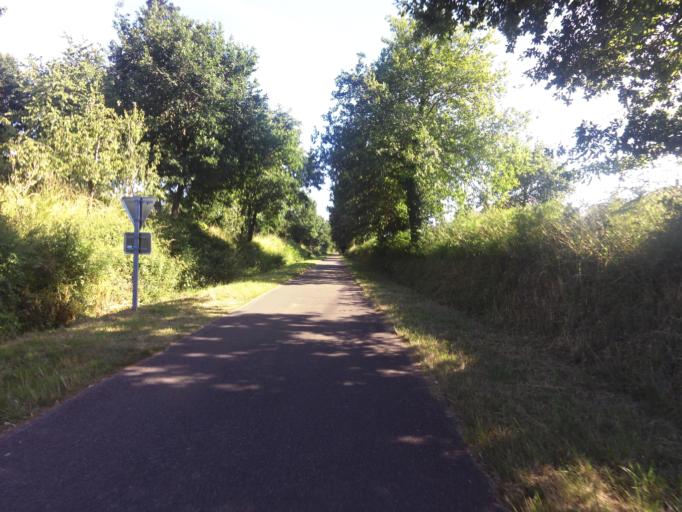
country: FR
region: Brittany
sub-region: Departement du Morbihan
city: Guillac
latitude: 47.8580
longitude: -2.4396
